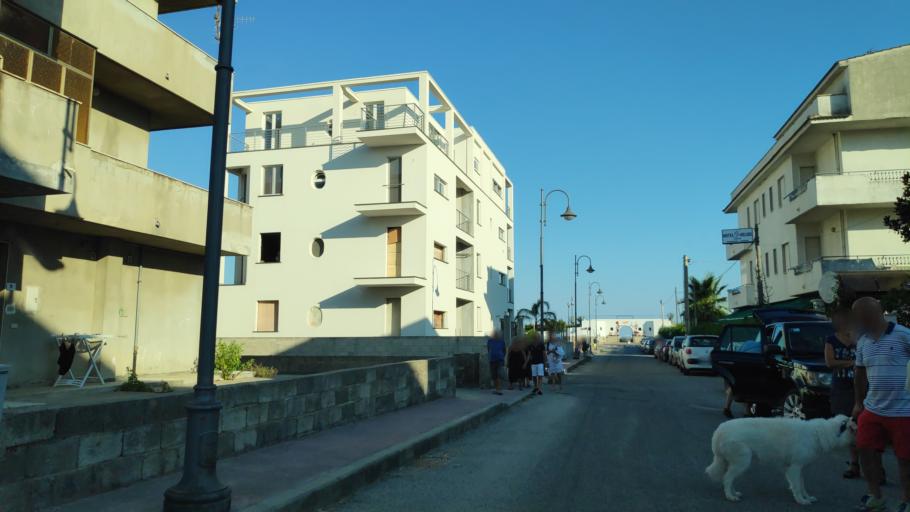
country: IT
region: Calabria
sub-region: Provincia di Reggio Calabria
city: Caulonia Marina
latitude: 38.3408
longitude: 16.4637
